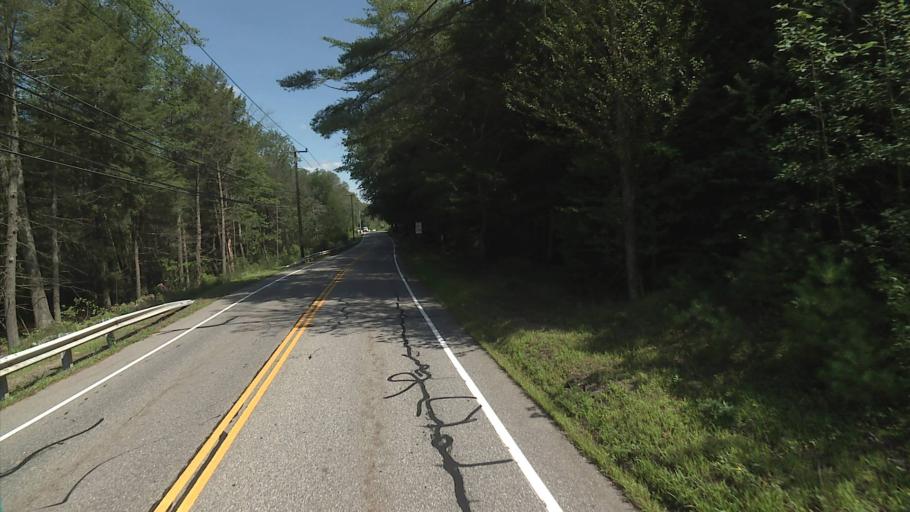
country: US
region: Connecticut
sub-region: Windham County
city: South Woodstock
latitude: 41.8862
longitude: -72.0823
